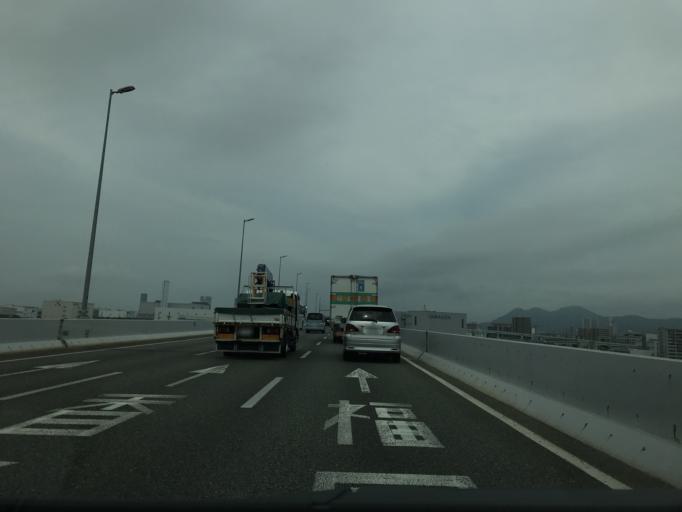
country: JP
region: Fukuoka
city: Fukuoka-shi
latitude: 33.6296
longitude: 130.4175
